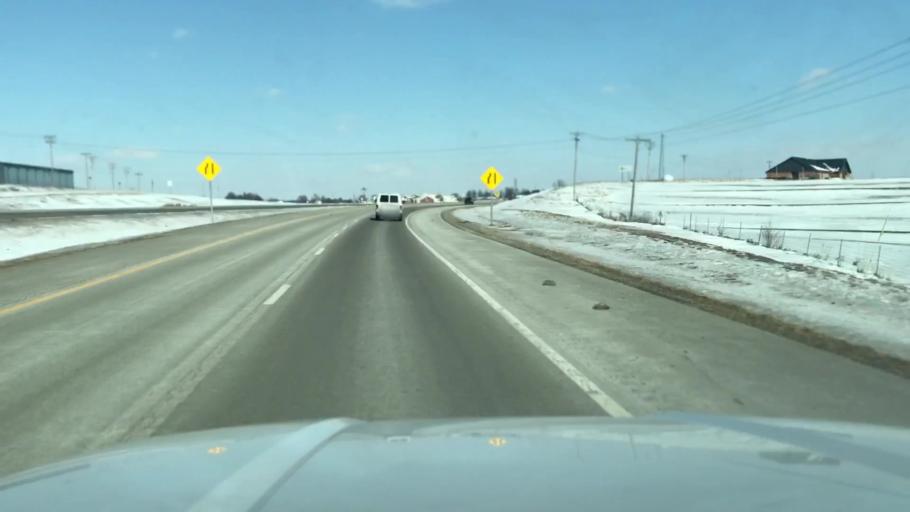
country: US
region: Missouri
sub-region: Nodaway County
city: Maryville
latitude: 40.3098
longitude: -94.8742
